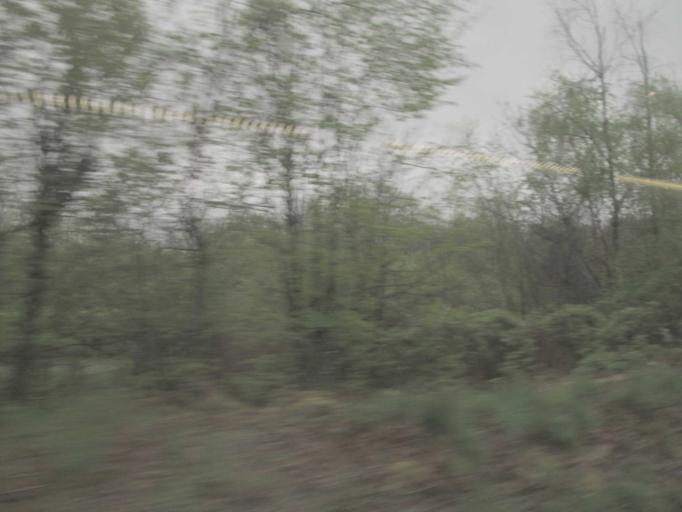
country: GB
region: England
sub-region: Hampshire
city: Yateley
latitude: 51.3576
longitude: -0.8139
